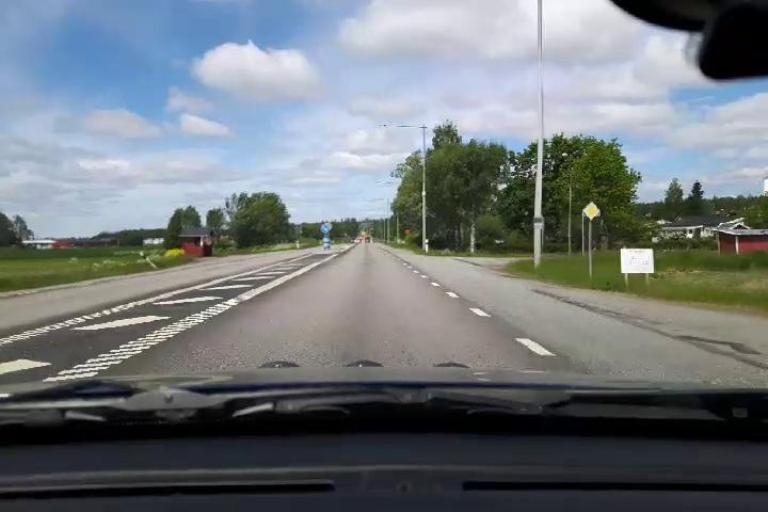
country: SE
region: Uppsala
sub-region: Osthammars Kommun
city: Bjorklinge
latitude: 60.0191
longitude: 17.5561
